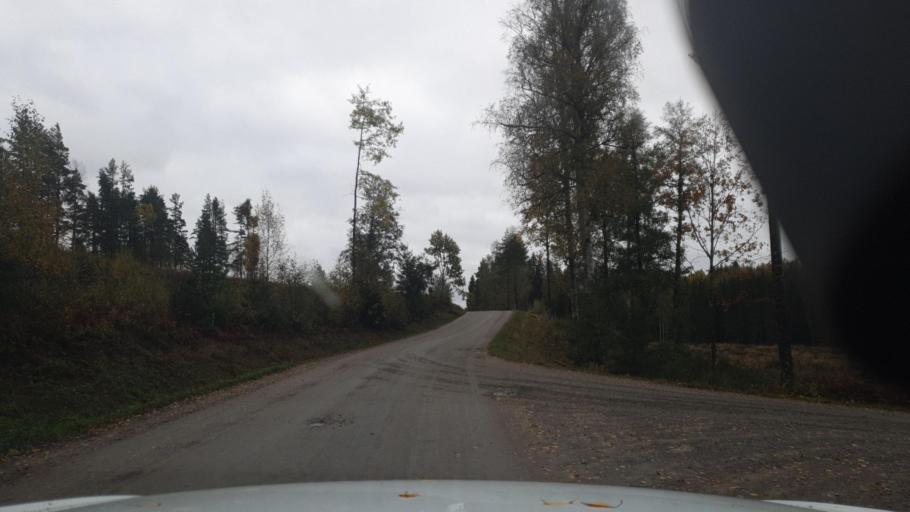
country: SE
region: Vaermland
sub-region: Karlstads Kommun
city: Edsvalla
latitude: 59.4942
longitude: 13.0296
